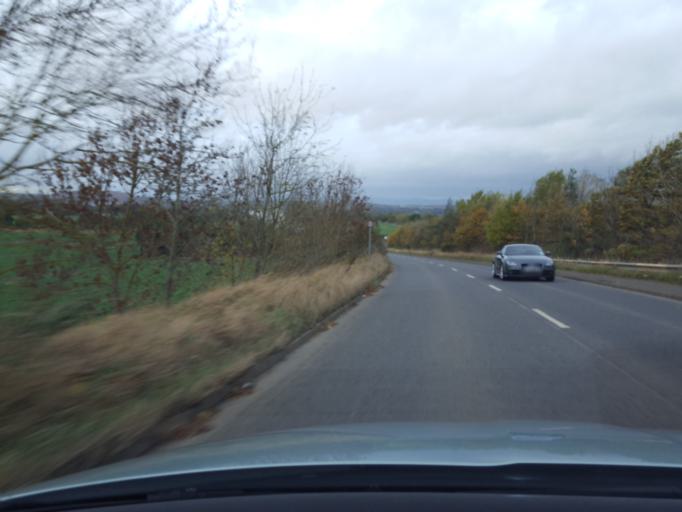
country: GB
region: Scotland
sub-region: Edinburgh
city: Newbridge
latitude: 55.9128
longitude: -3.4070
